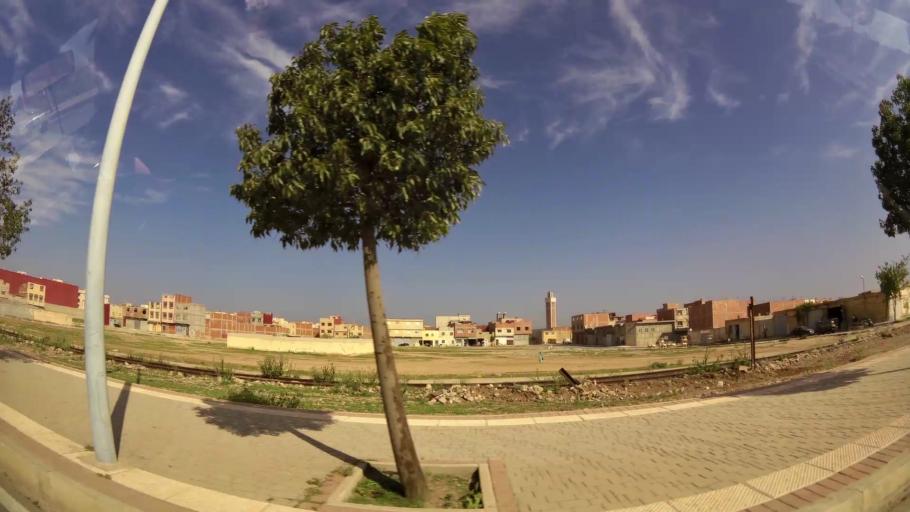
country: MA
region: Oriental
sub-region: Oujda-Angad
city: Oujda
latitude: 34.7141
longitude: -1.8853
